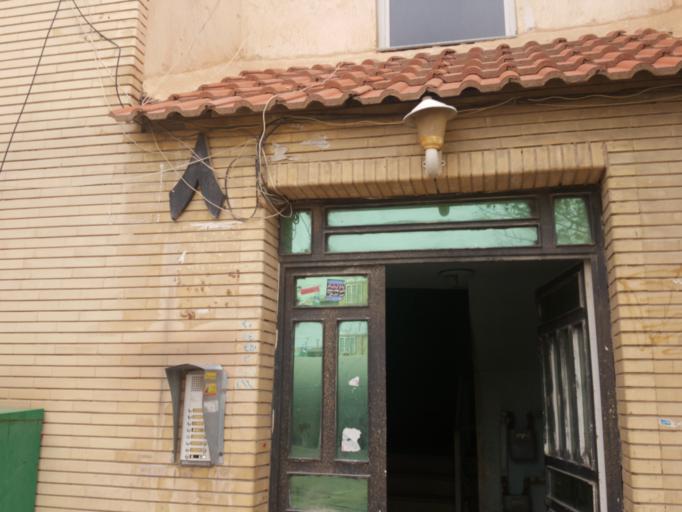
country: IR
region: Fars
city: Marvdasht
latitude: 29.8704
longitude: 52.8237
